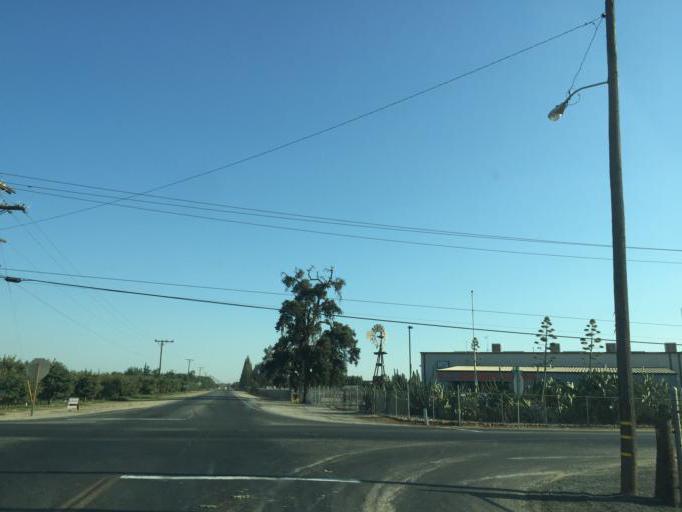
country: US
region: California
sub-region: Tulare County
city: Visalia
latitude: 36.3859
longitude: -119.2788
